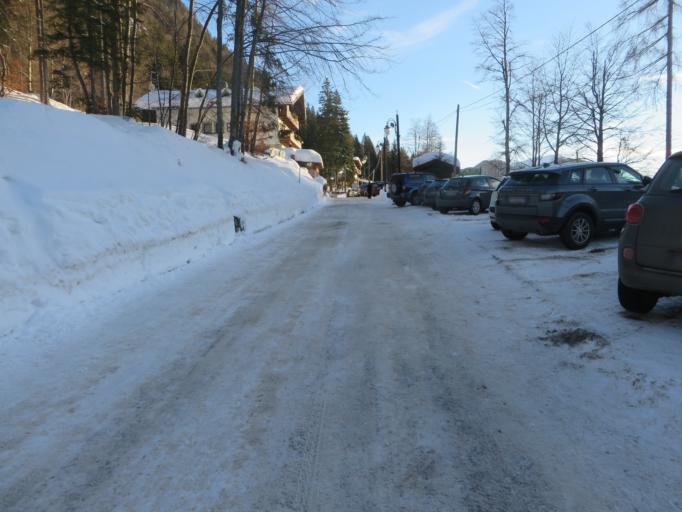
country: IT
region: Trentino-Alto Adige
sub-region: Provincia di Trento
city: Carisolo
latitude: 46.2212
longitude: 10.8283
